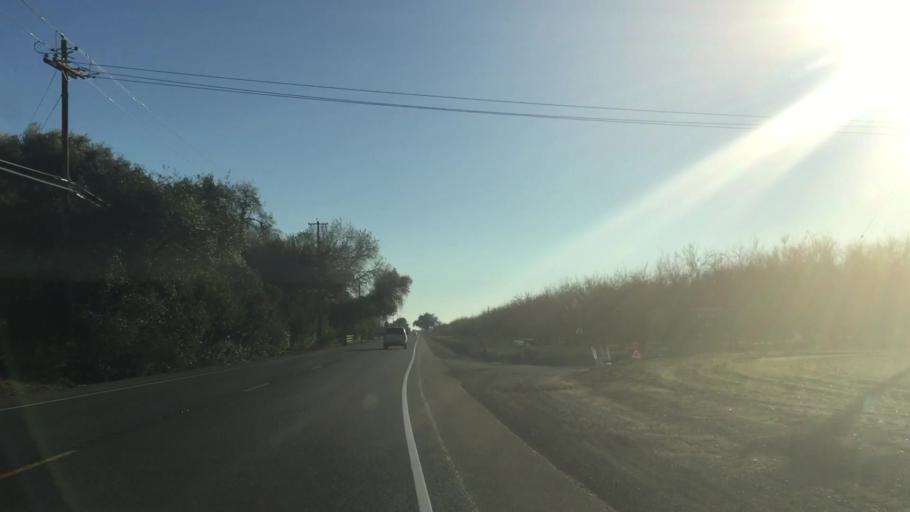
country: US
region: California
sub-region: Sutter County
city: Live Oak
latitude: 39.2724
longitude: -121.5959
